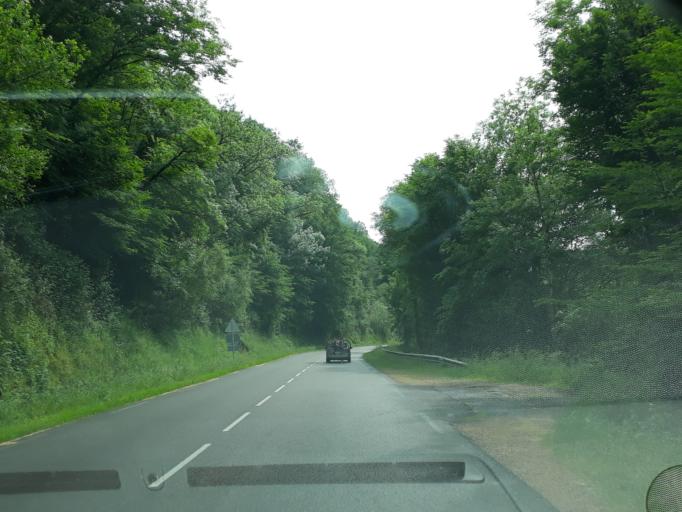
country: FR
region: Limousin
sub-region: Departement de la Correze
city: Beynat
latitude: 45.1320
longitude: 1.6733
